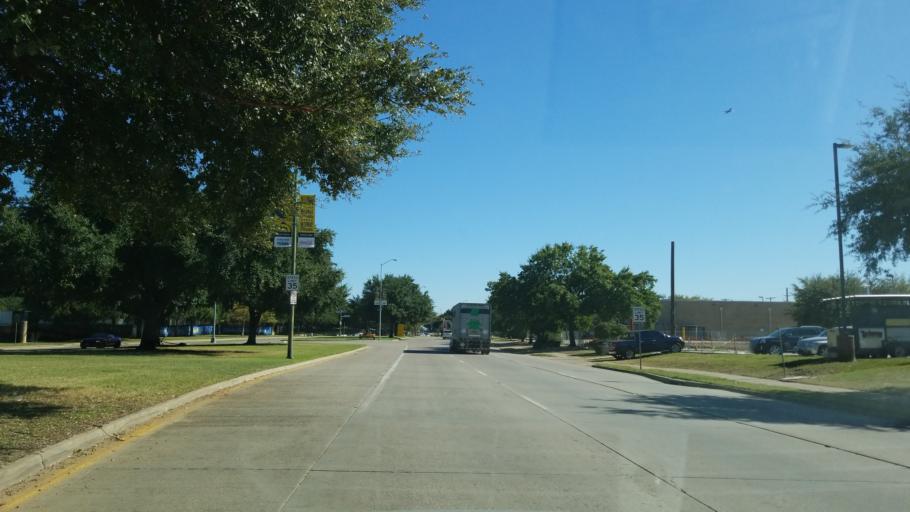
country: US
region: Texas
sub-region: Dallas County
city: Dallas
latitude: 32.7763
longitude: -96.7638
